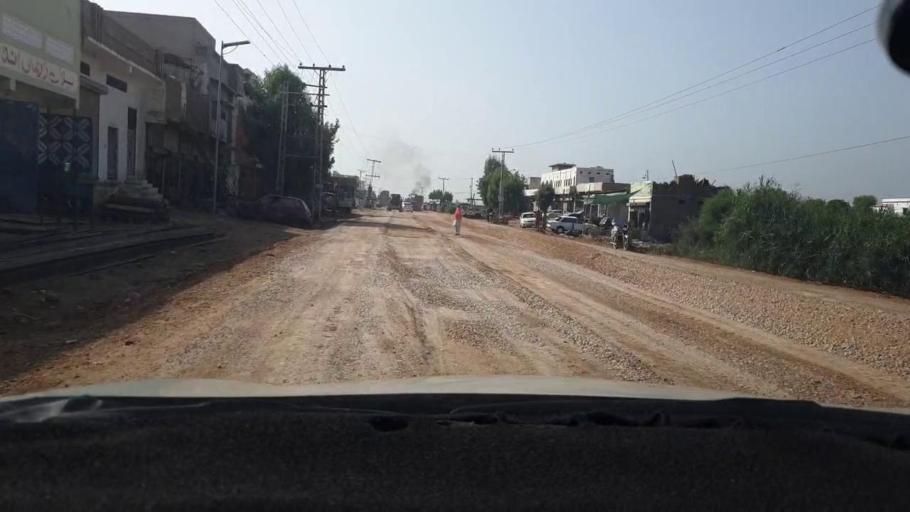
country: PK
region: Sindh
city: Sanghar
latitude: 26.0369
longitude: 68.9512
